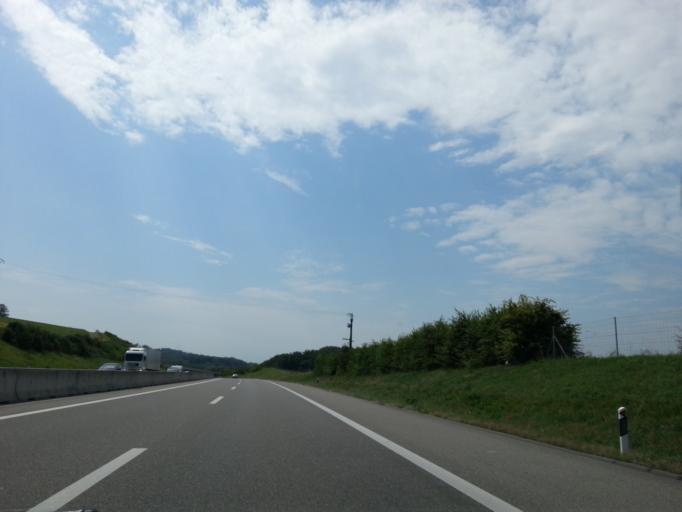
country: CH
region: Fribourg
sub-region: See District
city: Kerzers
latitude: 46.9576
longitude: 7.1709
